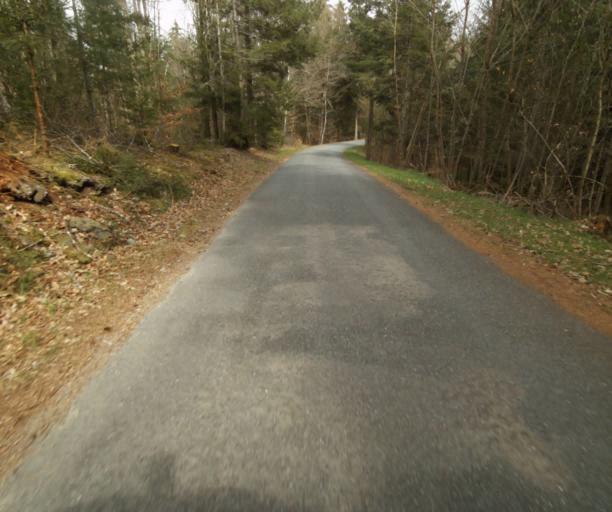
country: FR
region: Limousin
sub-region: Departement de la Correze
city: Correze
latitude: 45.2900
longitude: 1.9586
